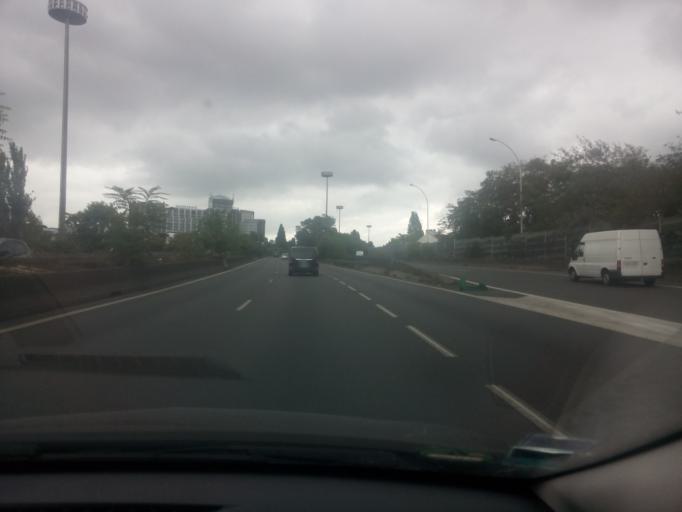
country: FR
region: Ile-de-France
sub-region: Departement du Val-de-Marne
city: Cachan
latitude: 48.7989
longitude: 2.3425
